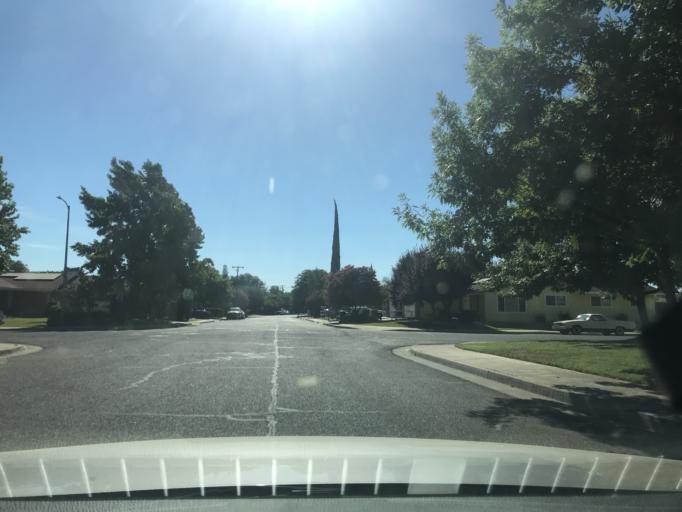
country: US
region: California
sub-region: Merced County
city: Atwater
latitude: 37.3480
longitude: -120.5886
